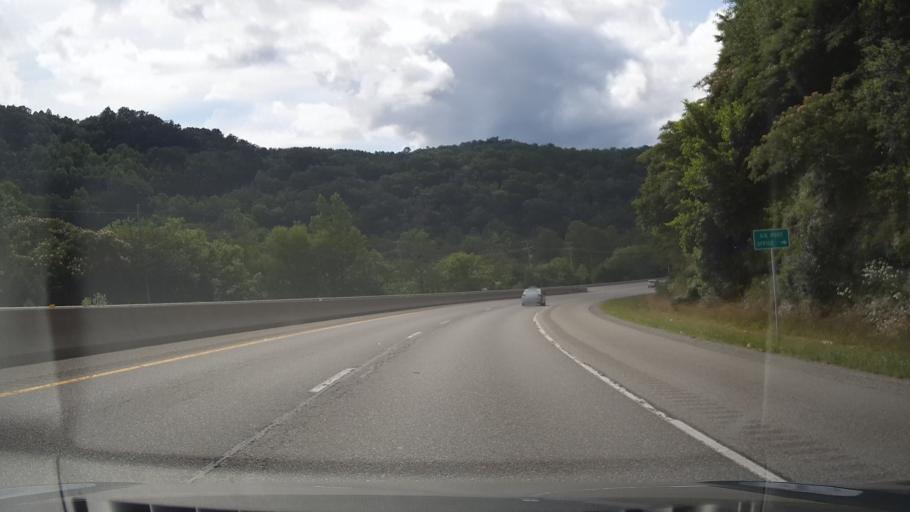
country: US
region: Kentucky
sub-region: Pike County
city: Coal Run Village
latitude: 37.5584
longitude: -82.6429
